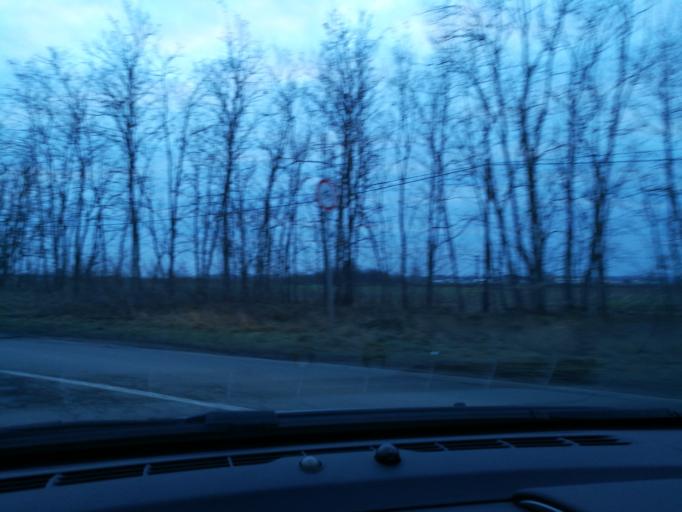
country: HU
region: Szabolcs-Szatmar-Bereg
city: Nyiregyhaza
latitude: 47.9830
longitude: 21.7046
